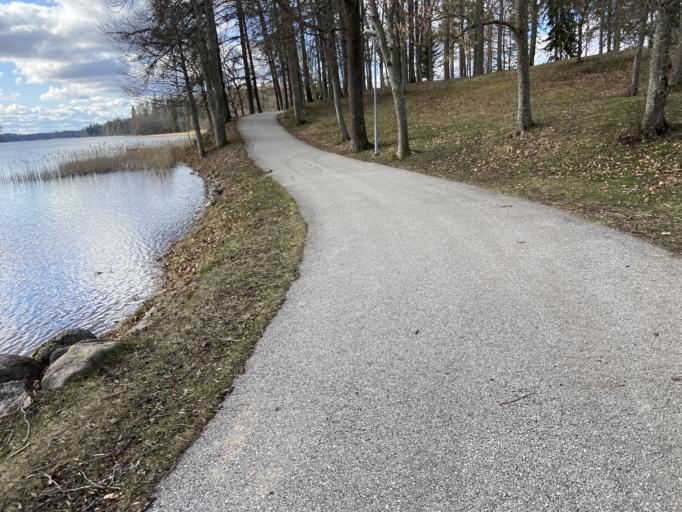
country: EE
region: Tartu
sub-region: Elva linn
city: Elva
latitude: 58.0453
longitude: 26.4612
